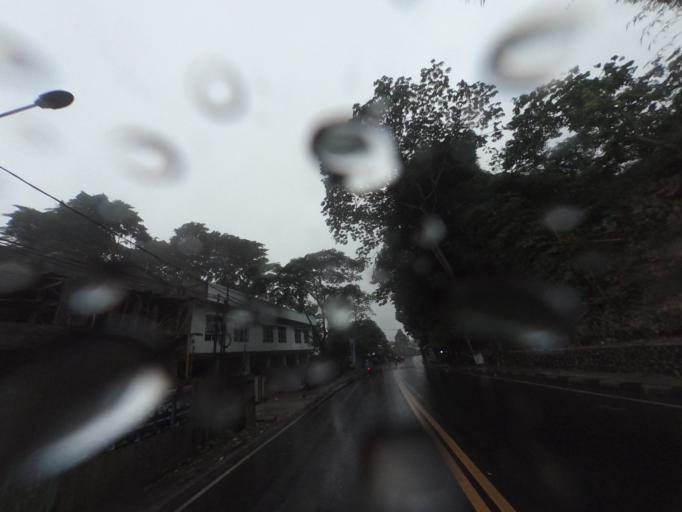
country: ID
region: West Java
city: Caringin
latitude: -6.6604
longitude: 106.8569
